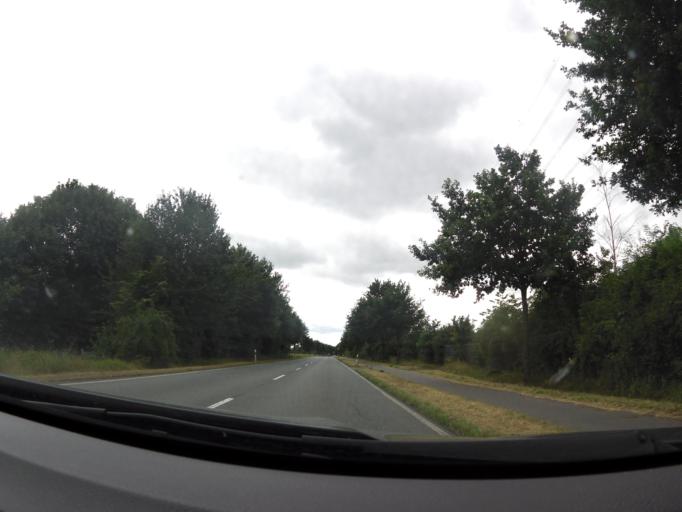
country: DE
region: North Rhine-Westphalia
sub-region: Regierungsbezirk Dusseldorf
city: Voerde
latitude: 51.6354
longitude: 6.6576
